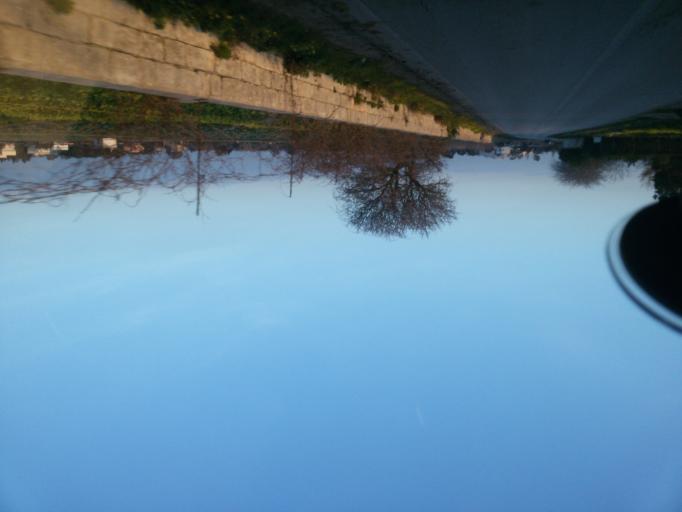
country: IT
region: Apulia
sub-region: Provincia di Brindisi
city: La Rosa
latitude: 40.6030
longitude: 17.9462
